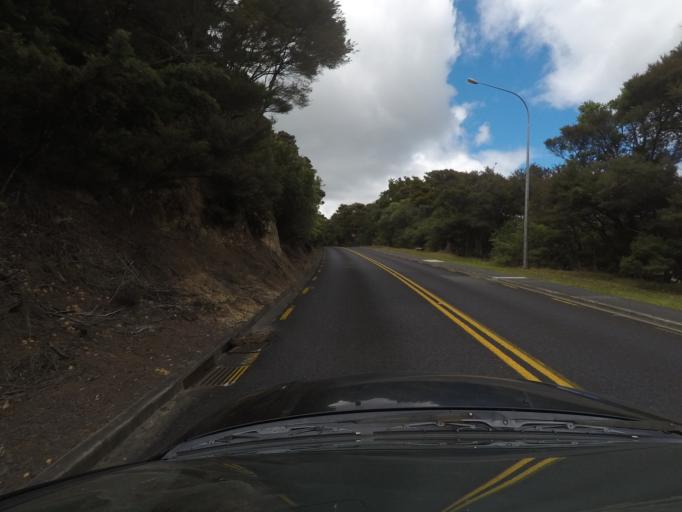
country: NZ
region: Northland
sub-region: Far North District
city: Paihia
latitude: -35.2886
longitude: 174.0963
